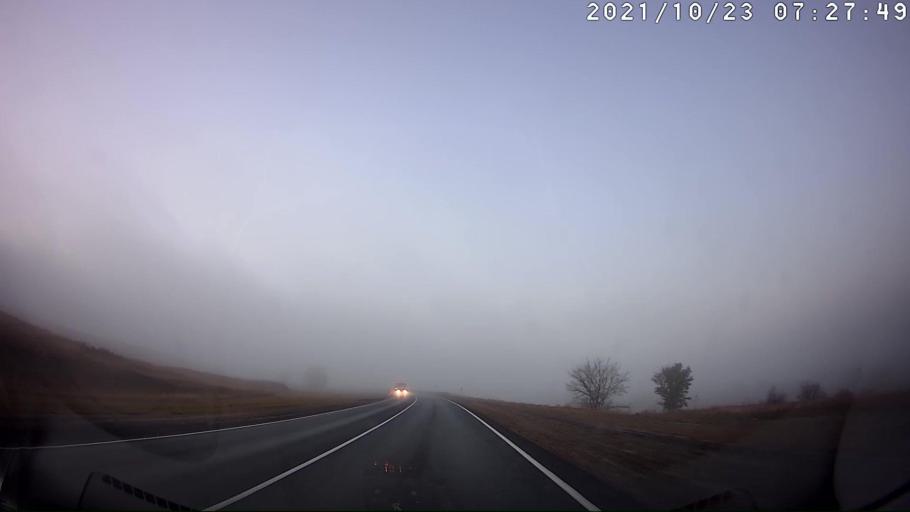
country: RU
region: Saratov
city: Alekseyevka
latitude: 52.3291
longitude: 47.9208
